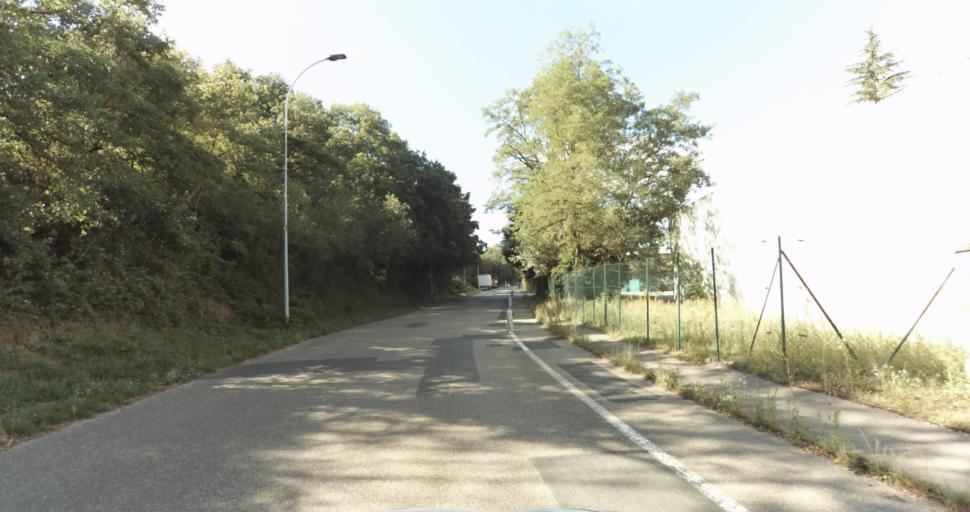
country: FR
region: Rhone-Alpes
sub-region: Departement du Rhone
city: Chaponost
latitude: 45.6945
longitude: 4.7616
